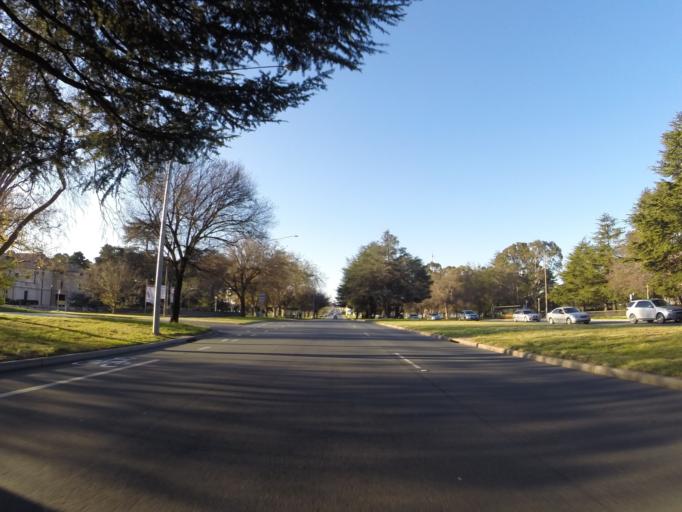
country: AU
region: Australian Capital Territory
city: Canberra
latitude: -35.2987
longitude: 149.1259
